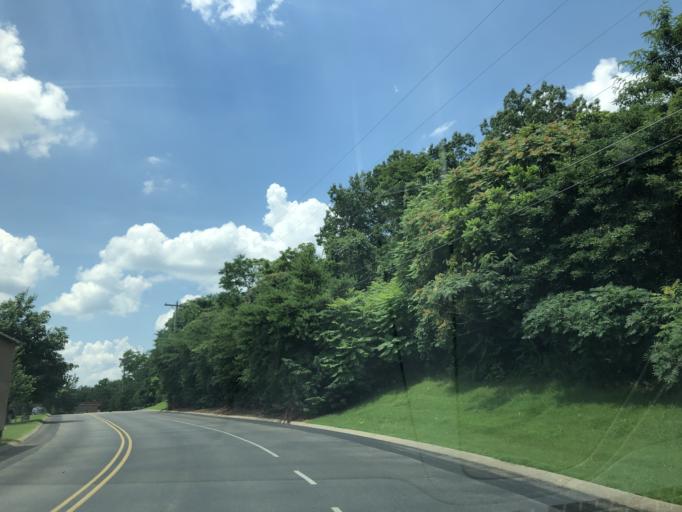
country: US
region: Tennessee
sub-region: Williamson County
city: Brentwood Estates
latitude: 36.0207
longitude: -86.7115
